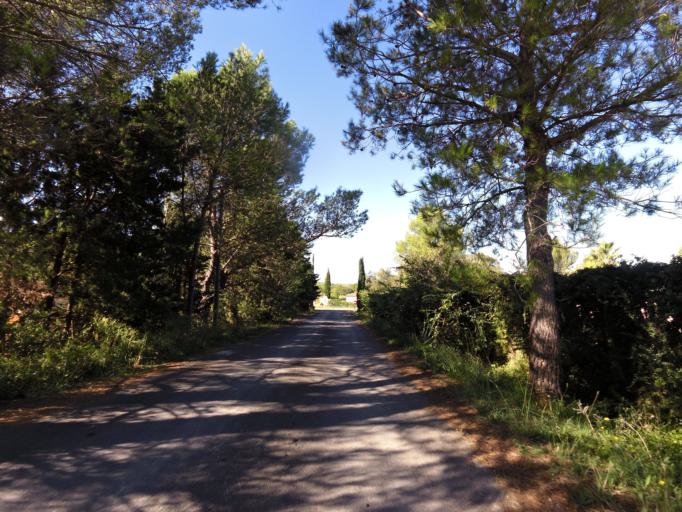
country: FR
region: Languedoc-Roussillon
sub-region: Departement du Gard
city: Aubais
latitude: 43.7418
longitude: 4.1463
